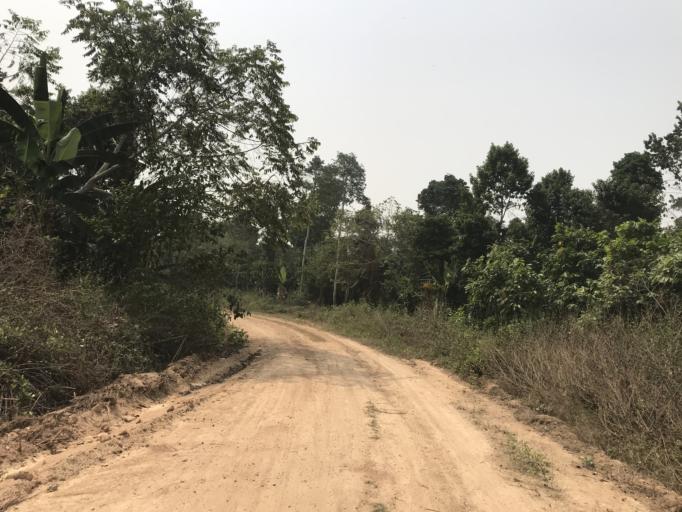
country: NG
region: Osun
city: Ifetedo
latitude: 7.0372
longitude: 4.4752
